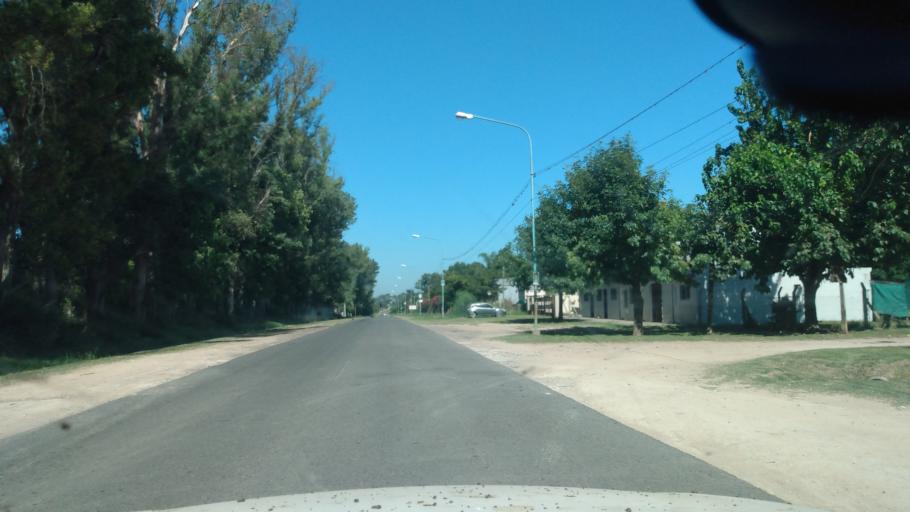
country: AR
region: Buenos Aires
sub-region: Partido de Lujan
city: Lujan
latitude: -34.5050
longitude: -59.0772
